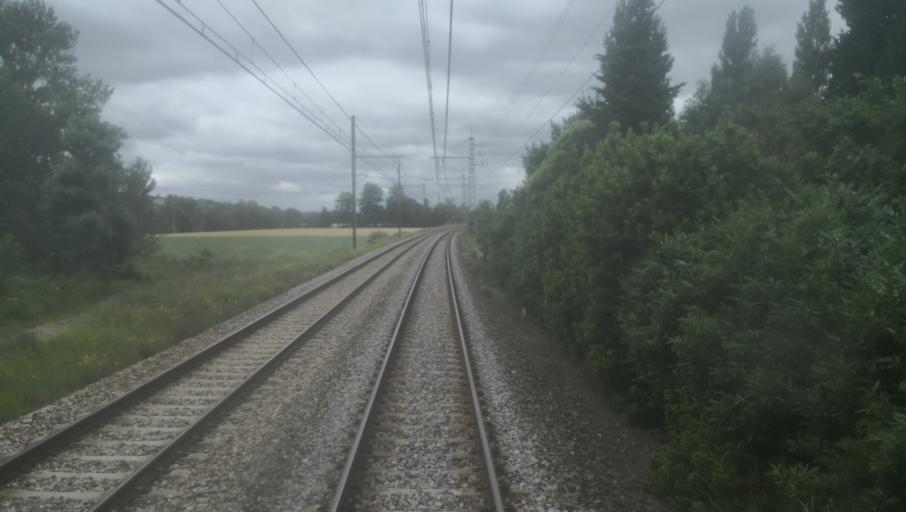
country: FR
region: Midi-Pyrenees
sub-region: Departement de la Haute-Garonne
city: Avignonet-Lauragais
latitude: 43.3696
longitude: 1.7686
